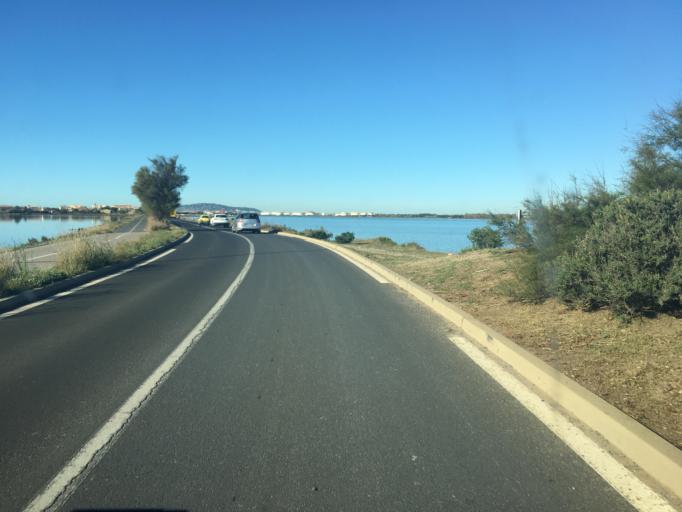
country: FR
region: Languedoc-Roussillon
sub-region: Departement de l'Herault
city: Frontignan
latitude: 43.4411
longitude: 3.7900
